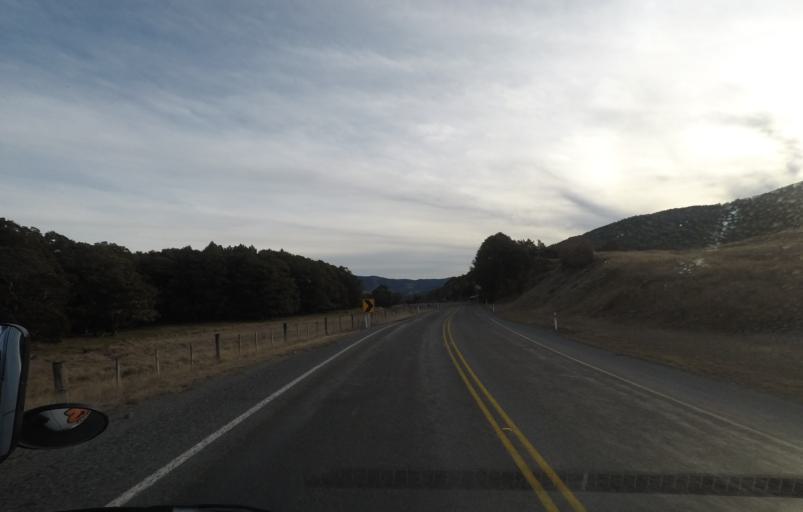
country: NZ
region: Tasman
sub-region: Tasman District
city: Wakefield
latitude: -41.7996
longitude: 172.8670
